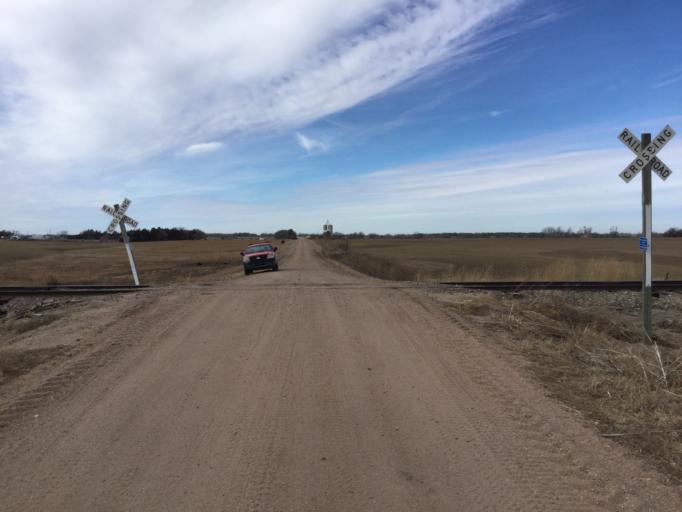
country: US
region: Kansas
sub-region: Rice County
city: Lyons
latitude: 38.4497
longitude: -98.1922
